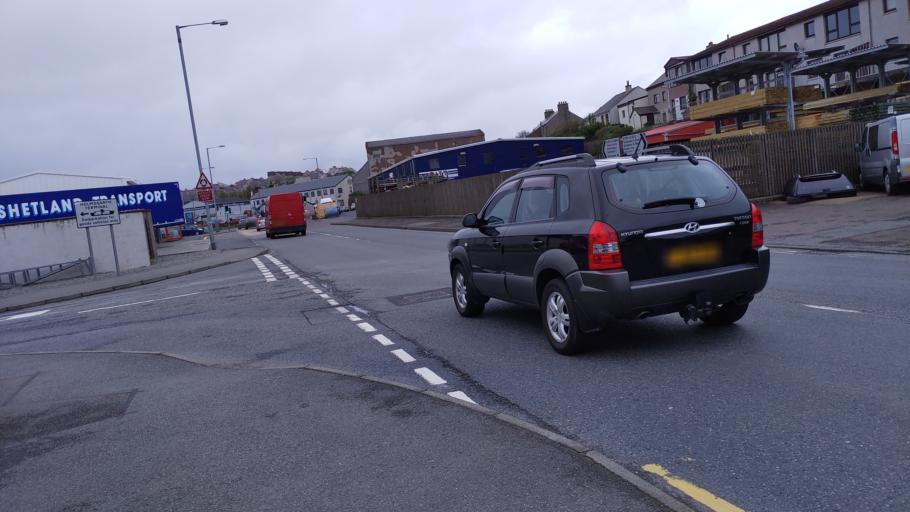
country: GB
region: Scotland
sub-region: Shetland Islands
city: Lerwick
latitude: 60.1601
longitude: -1.1573
